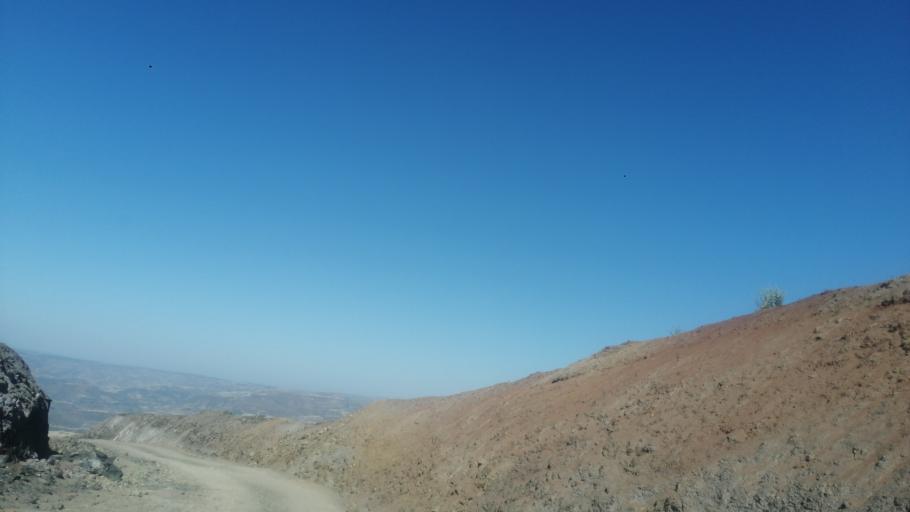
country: ET
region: Amhara
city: Addiet Canna
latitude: 11.1524
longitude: 37.8586
